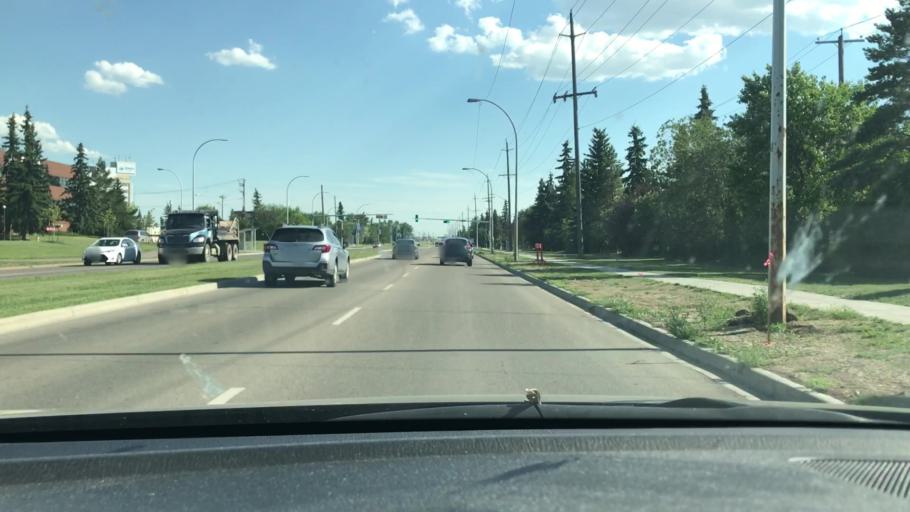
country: CA
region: Alberta
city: Edmonton
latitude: 53.5284
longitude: -113.4188
